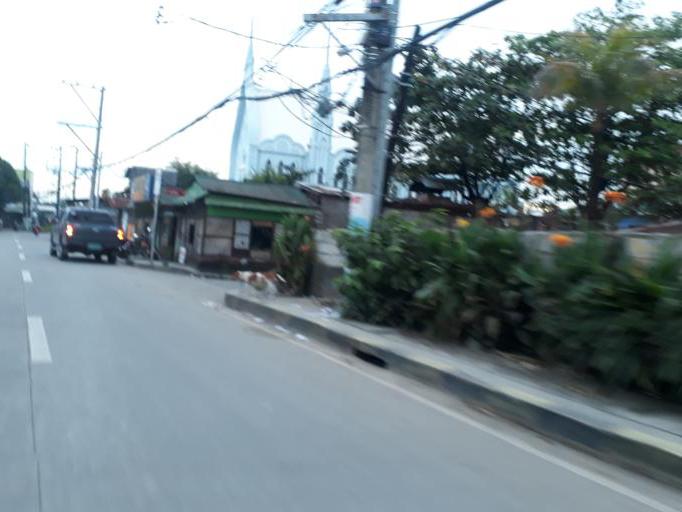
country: PH
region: Central Luzon
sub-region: Province of Bulacan
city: Obando
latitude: 14.7102
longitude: 120.9513
